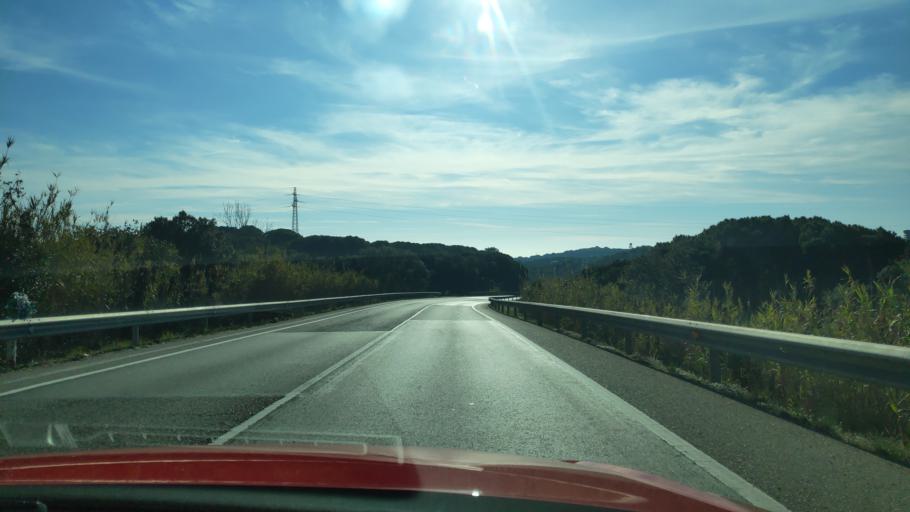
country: ES
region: Catalonia
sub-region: Provincia de Girona
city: Lloret de Mar
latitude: 41.7207
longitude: 2.8252
